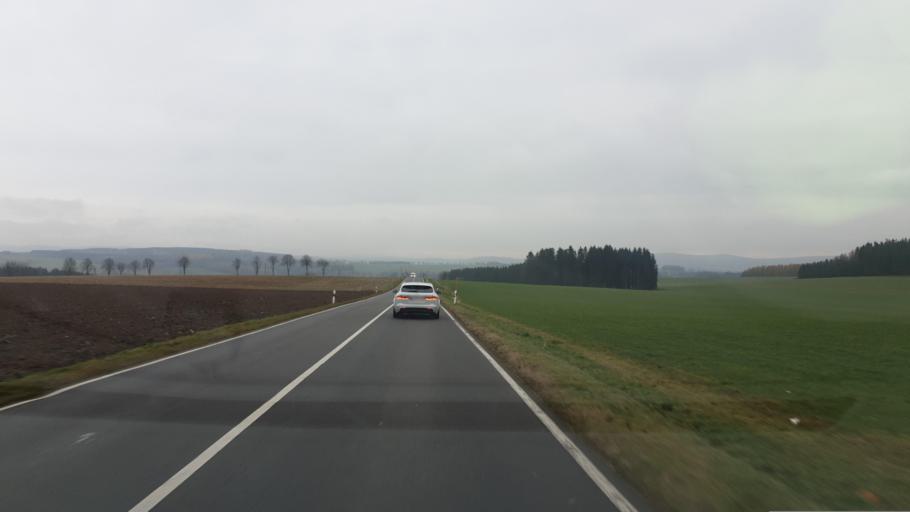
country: DE
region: Saxony
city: Pockau
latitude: 50.7384
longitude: 13.2781
